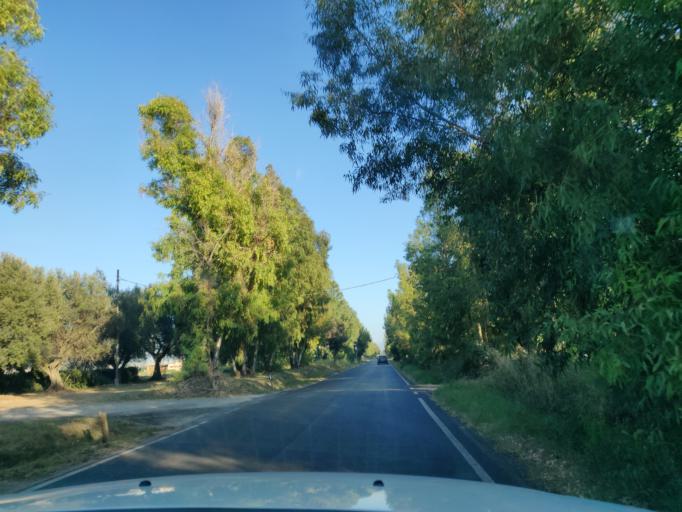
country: IT
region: Latium
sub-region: Provincia di Viterbo
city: Tarquinia
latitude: 42.2790
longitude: 11.6764
